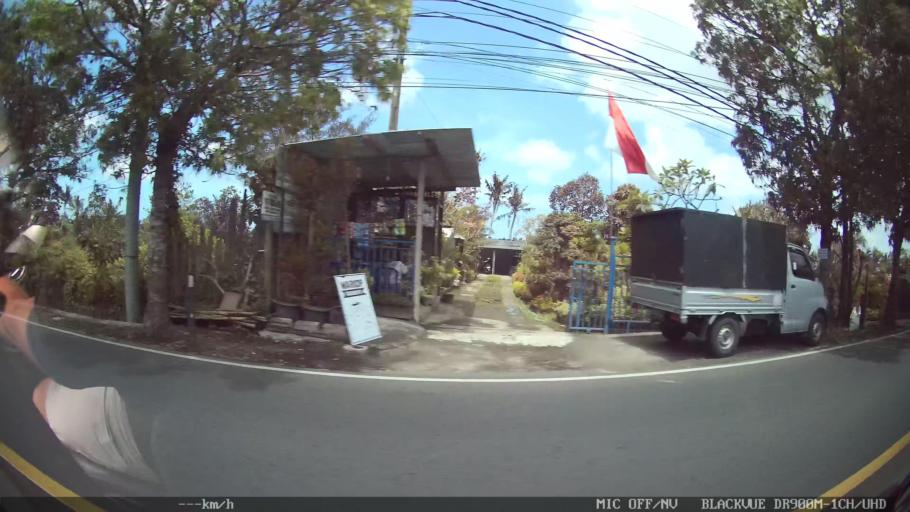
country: ID
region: Bali
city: Banjar Sedang
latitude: -8.5631
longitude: 115.2796
